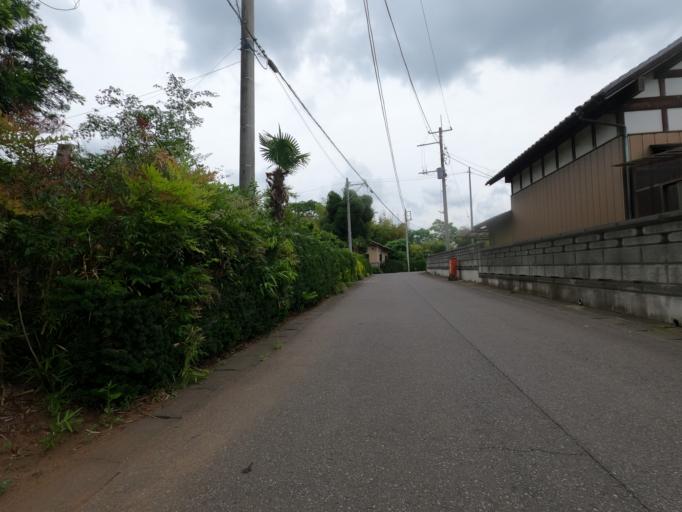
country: JP
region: Ibaraki
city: Moriya
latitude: 35.9535
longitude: 139.9694
